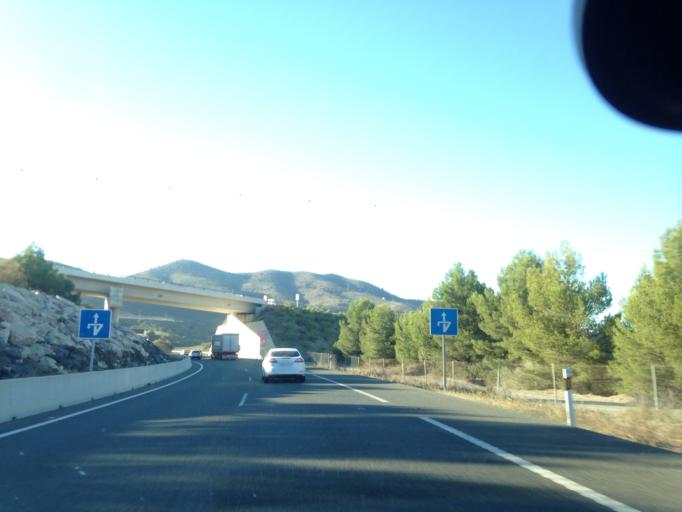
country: ES
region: Andalusia
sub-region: Provincia de Malaga
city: Casabermeja
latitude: 36.9092
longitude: -4.4461
